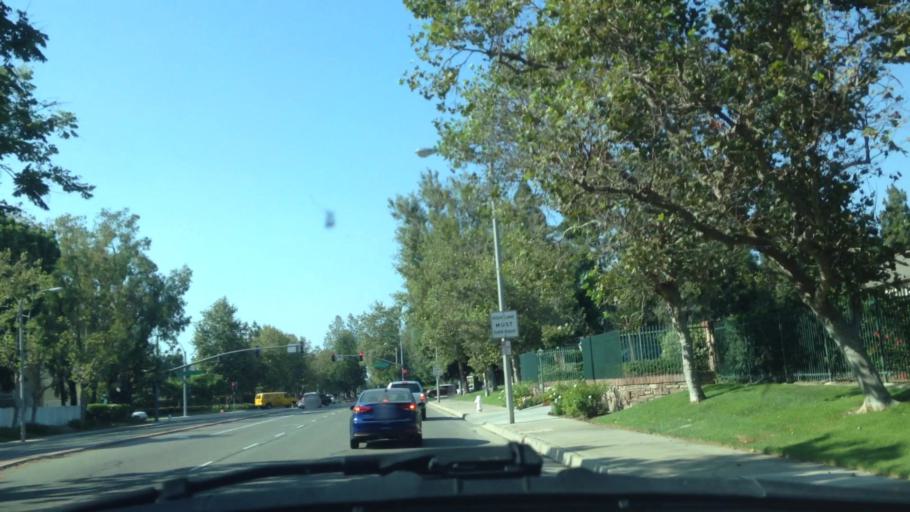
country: US
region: California
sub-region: Orange County
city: Santa Ana
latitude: 33.6989
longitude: -117.8921
